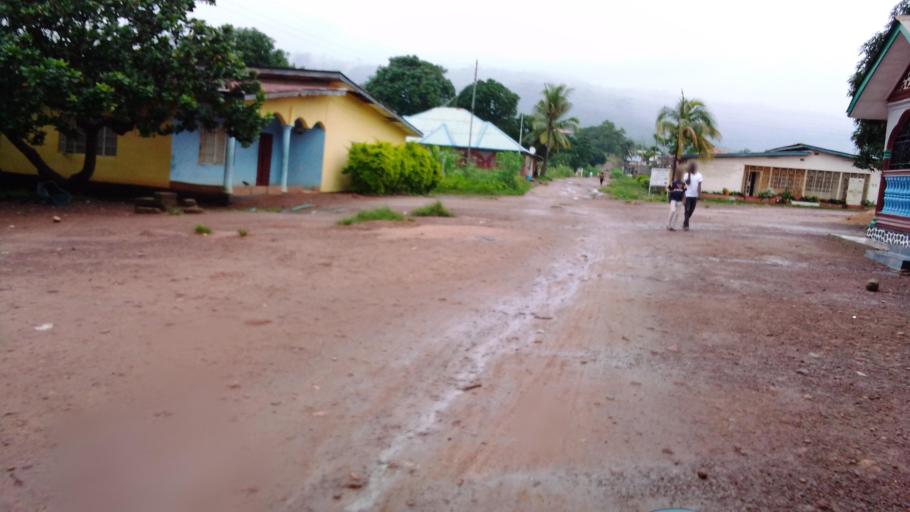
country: SL
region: Eastern Province
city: Kenema
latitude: 7.8963
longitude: -11.1793
